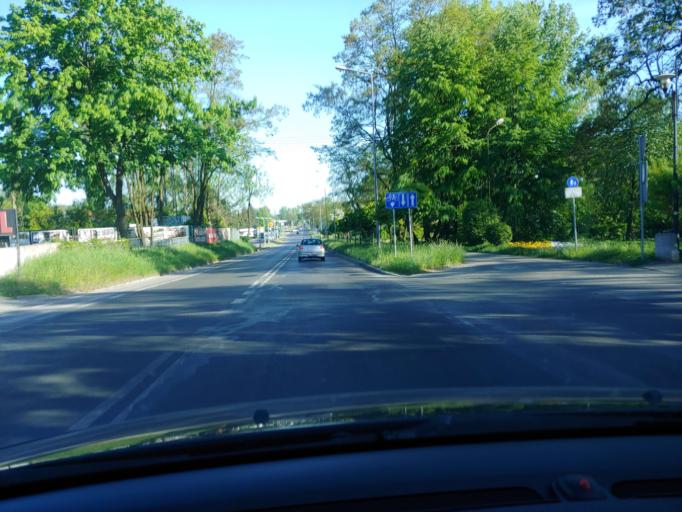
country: PL
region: Silesian Voivodeship
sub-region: Jaworzno
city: Jaworzno
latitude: 50.1958
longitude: 19.2821
